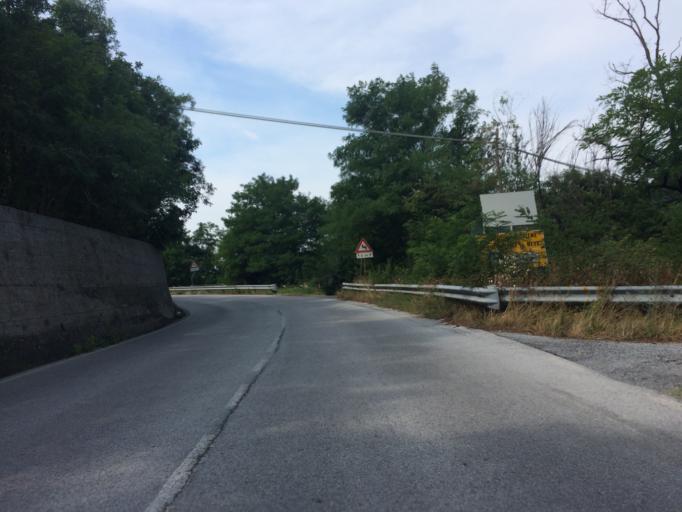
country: IT
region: Liguria
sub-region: Provincia di Savona
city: San Giovanni
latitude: 44.4040
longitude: 8.4900
